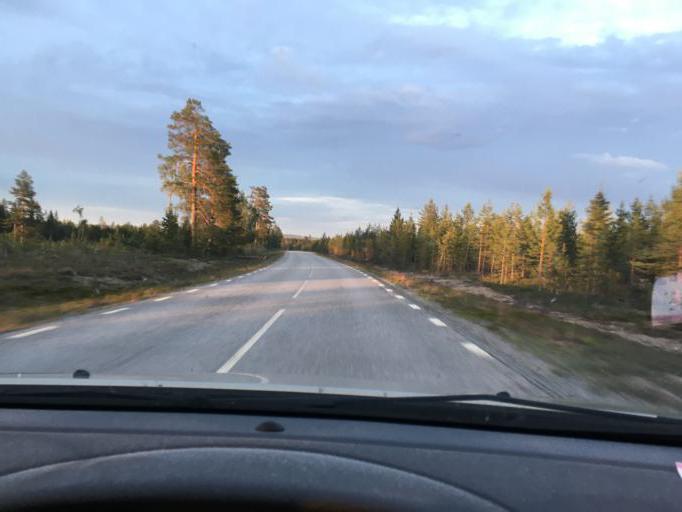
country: SE
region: Norrbotten
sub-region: Kalix Kommun
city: Toere
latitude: 66.0545
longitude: 22.4609
